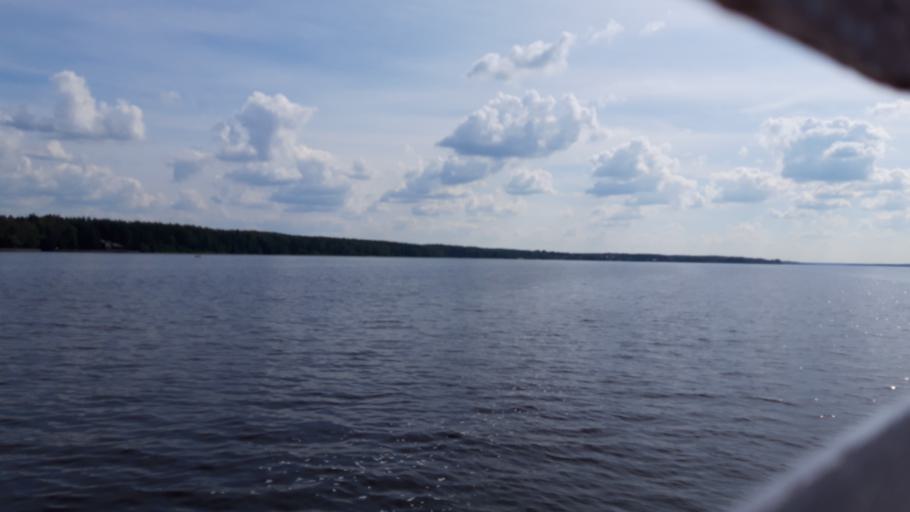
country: RU
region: Tverskaya
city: Konakovo
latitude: 56.6865
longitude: 36.6878
